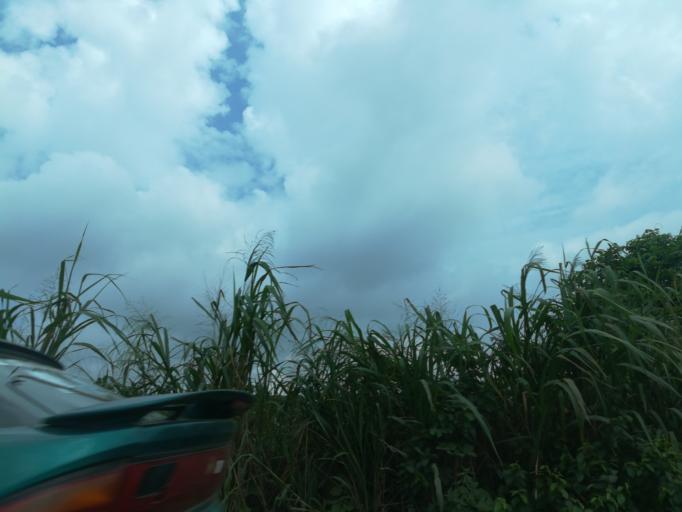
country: NG
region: Lagos
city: Ikorodu
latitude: 6.6598
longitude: 3.5870
